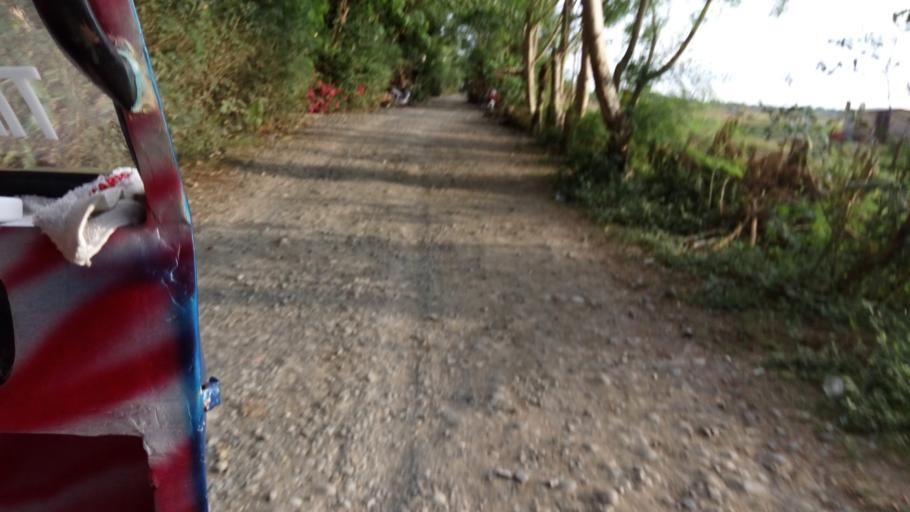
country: PH
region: Ilocos
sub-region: Province of La Union
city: Santo Tomas
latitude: 16.2814
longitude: 120.3851
